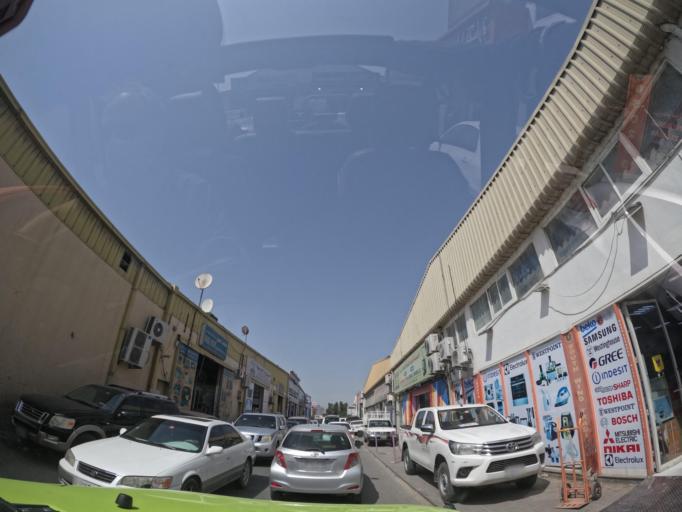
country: AE
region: Ash Shariqah
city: Sharjah
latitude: 25.3181
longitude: 55.4145
